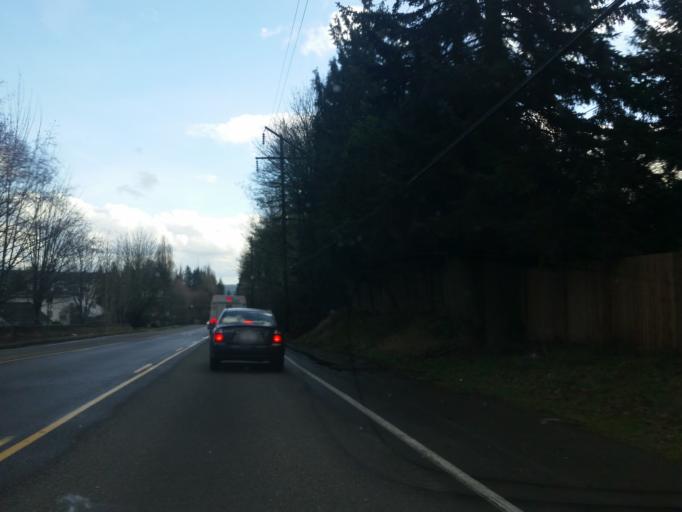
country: US
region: Washington
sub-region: Snohomish County
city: Mountlake Terrace
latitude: 47.7719
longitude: -122.3054
